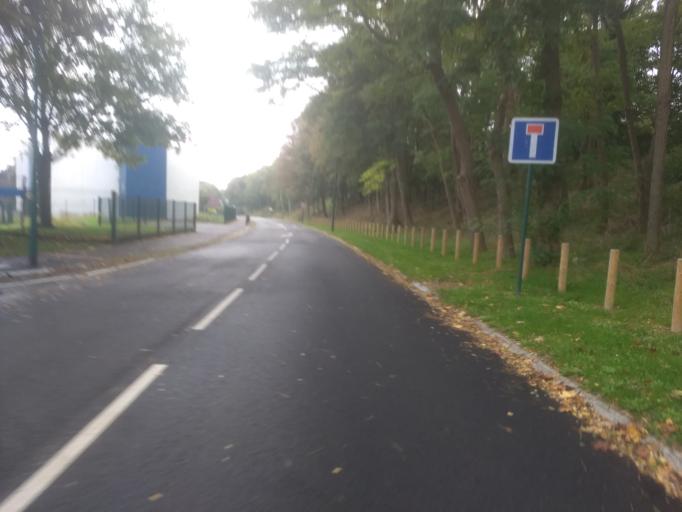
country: FR
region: Nord-Pas-de-Calais
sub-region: Departement du Pas-de-Calais
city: Saint-Nicolas
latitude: 50.3060
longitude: 2.7869
